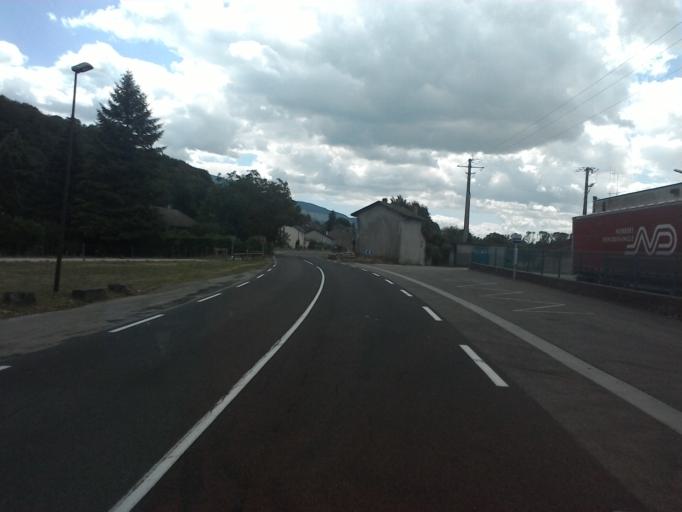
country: FR
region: Rhone-Alpes
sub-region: Departement de l'Ain
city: Sault-Brenaz
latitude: 45.8663
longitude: 5.3932
